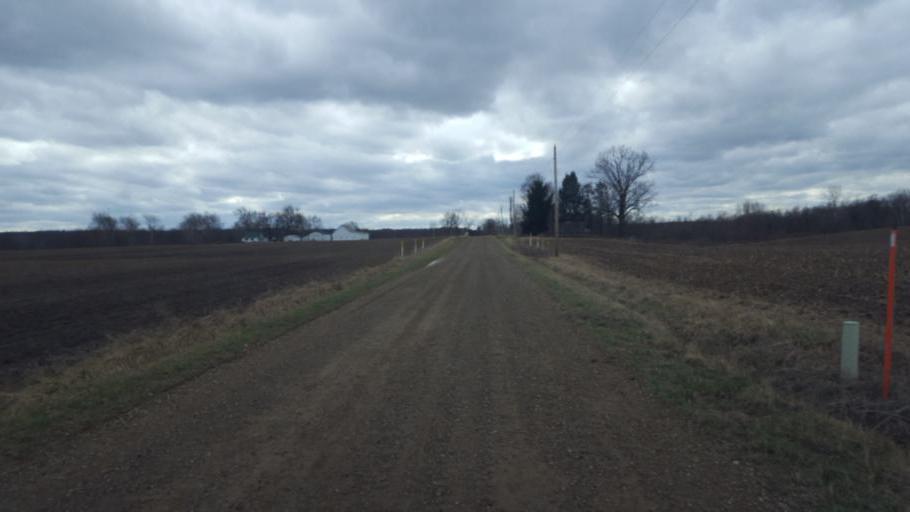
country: US
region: Ohio
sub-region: Licking County
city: Utica
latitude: 40.2712
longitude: -82.4977
